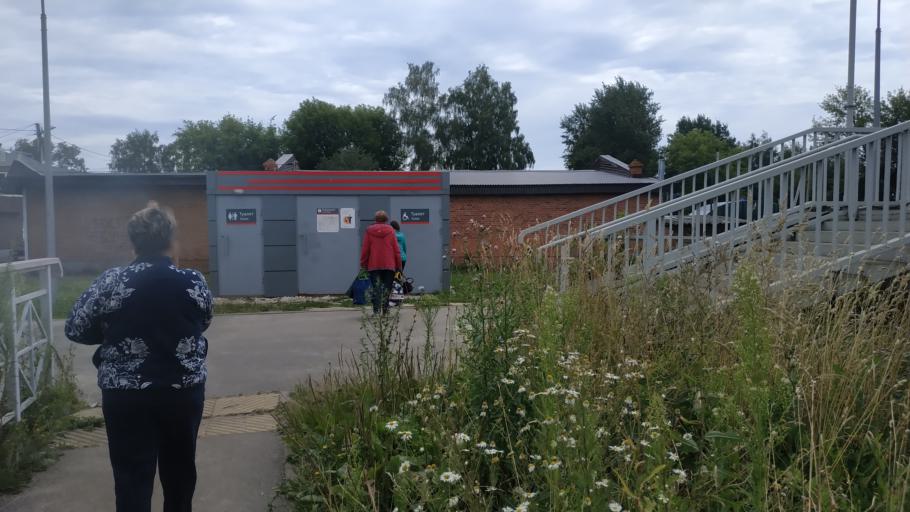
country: RU
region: Moskovskaya
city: Beloomut
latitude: 54.9159
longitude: 39.2589
